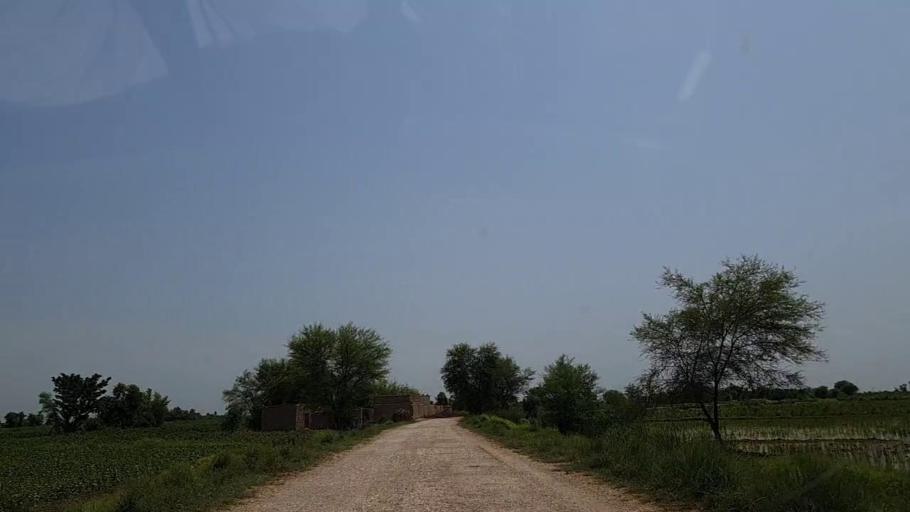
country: PK
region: Sindh
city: Ghotki
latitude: 27.9809
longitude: 69.4030
